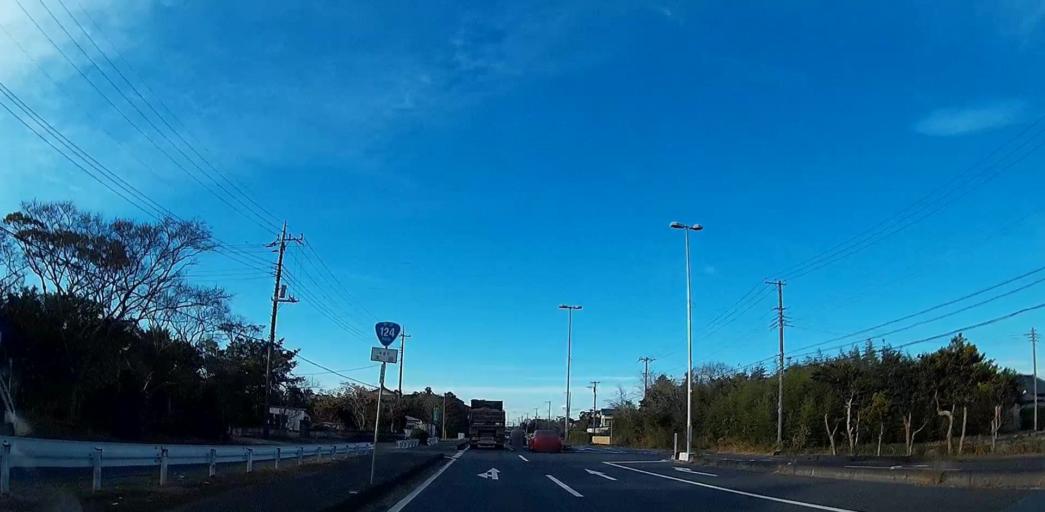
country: JP
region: Chiba
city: Omigawa
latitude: 35.8317
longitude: 140.7202
